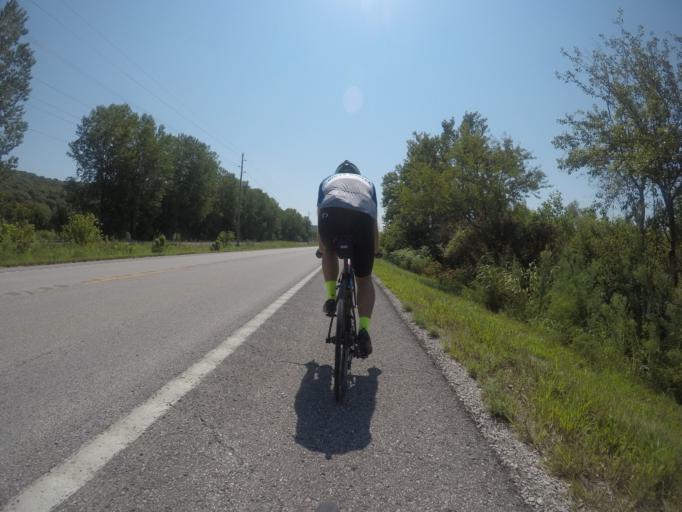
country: US
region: Kansas
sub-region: Atchison County
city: Atchison
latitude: 39.5012
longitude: -95.0069
